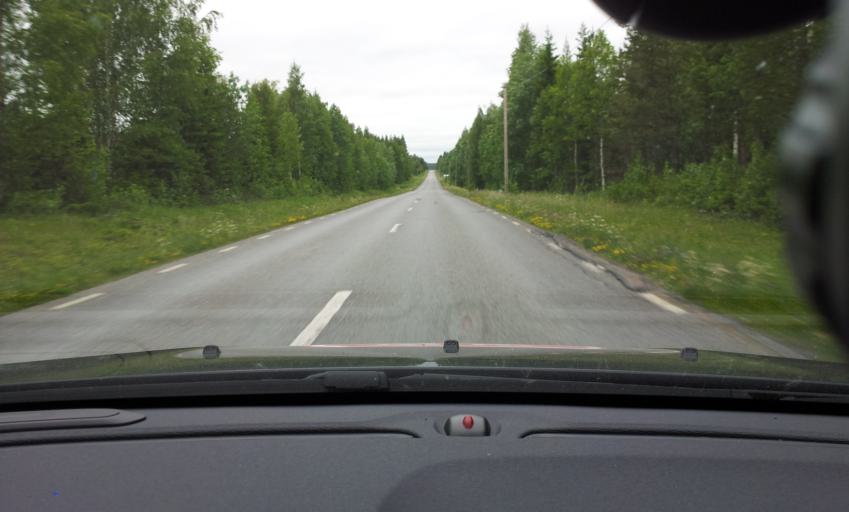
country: SE
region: Jaemtland
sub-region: Krokoms Kommun
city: Krokom
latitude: 63.1911
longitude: 14.0588
